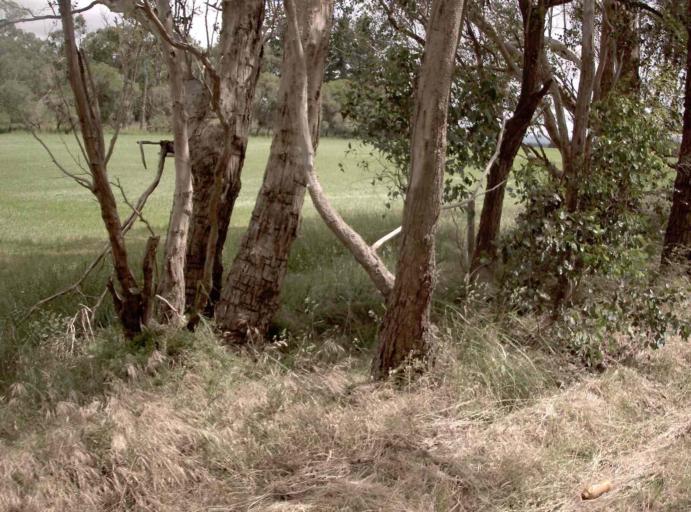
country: AU
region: Victoria
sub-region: Latrobe
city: Moe
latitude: -38.1214
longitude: 146.1479
